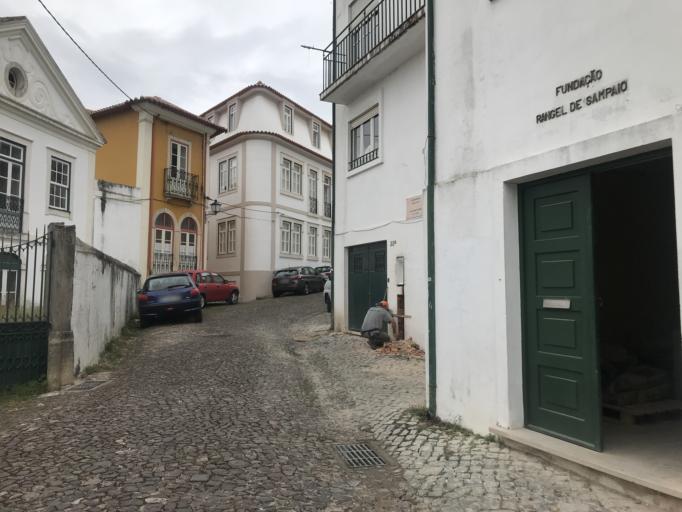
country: PT
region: Coimbra
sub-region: Coimbra
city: Coimbra
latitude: 40.2103
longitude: -8.4271
